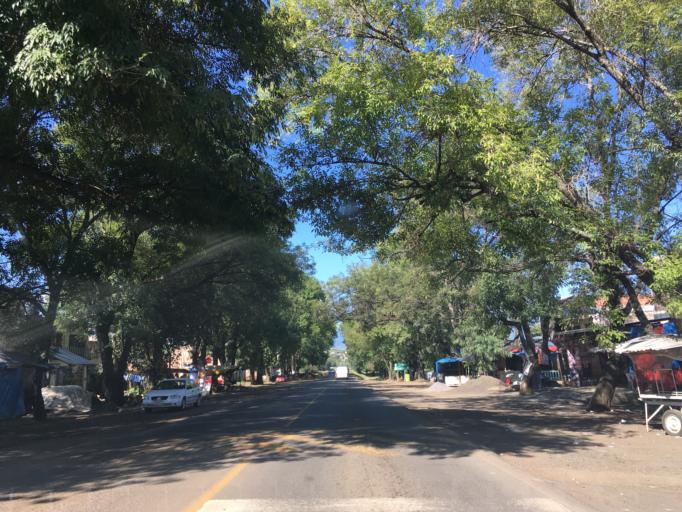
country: MX
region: Mexico
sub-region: Chalco
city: Los Nogales
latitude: 19.8598
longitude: -102.1558
